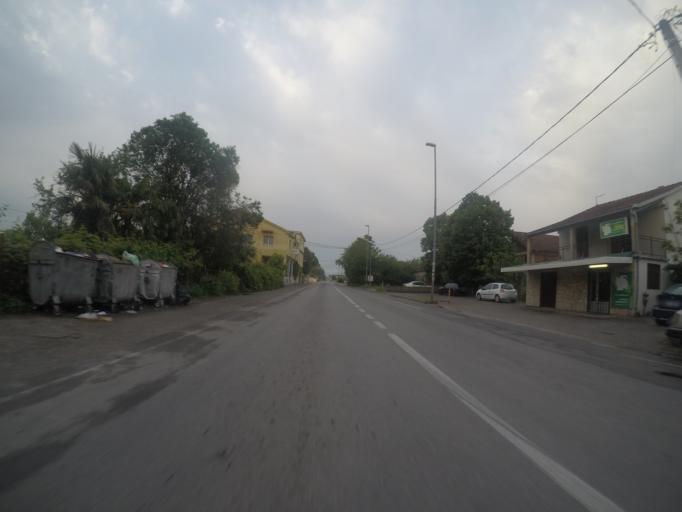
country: ME
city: Golubovci
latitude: 42.3298
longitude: 19.2204
